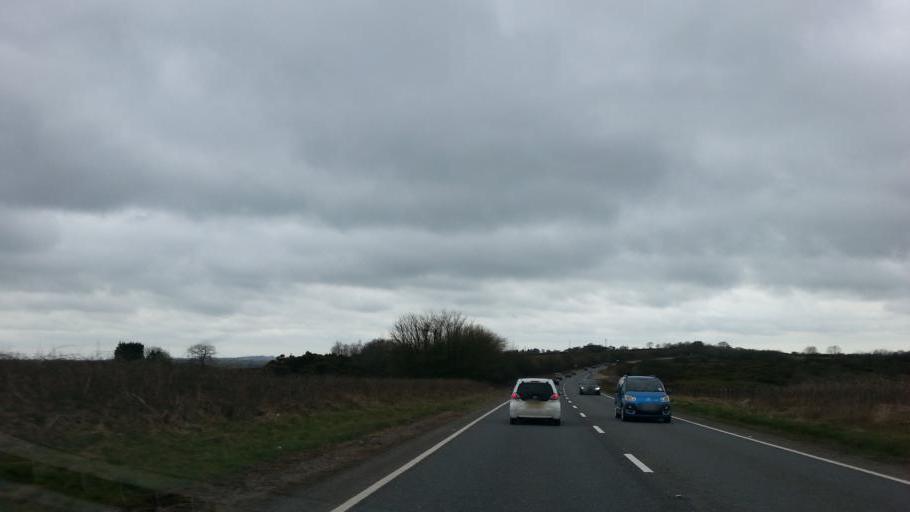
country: GB
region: England
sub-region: Devon
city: South Molton
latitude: 50.9821
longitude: -3.6865
